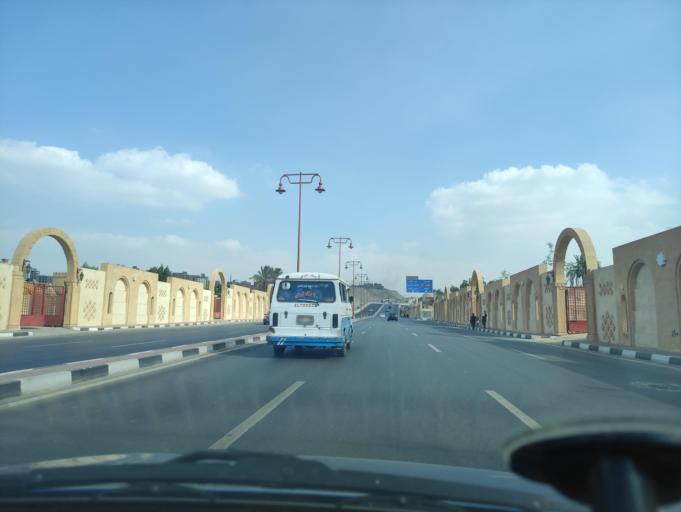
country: EG
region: Muhafazat al Qahirah
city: Cairo
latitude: 30.0528
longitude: 31.2827
